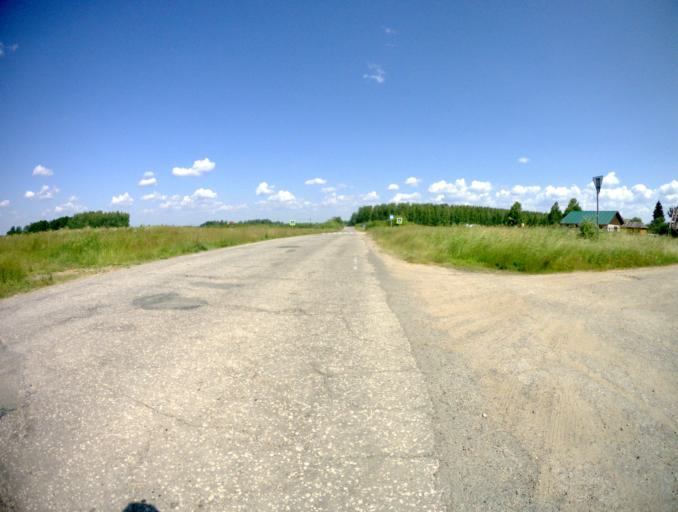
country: RU
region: Vladimir
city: Vyazniki
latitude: 56.2703
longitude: 42.1719
